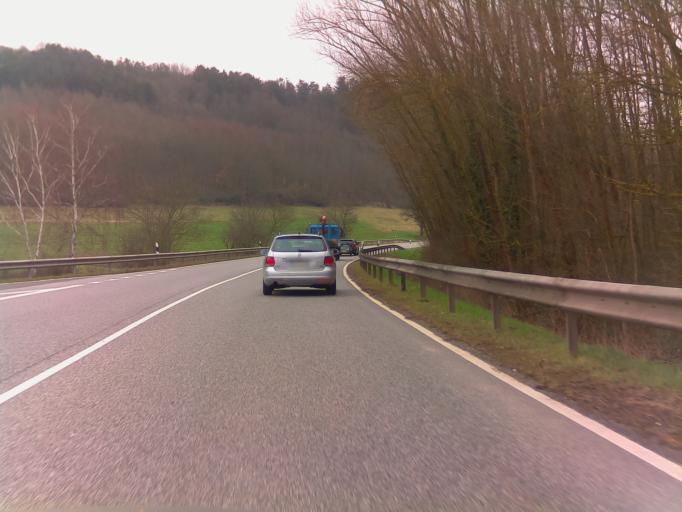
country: DE
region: Rheinland-Pfalz
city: Niedermoschel
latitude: 49.7323
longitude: 7.7991
